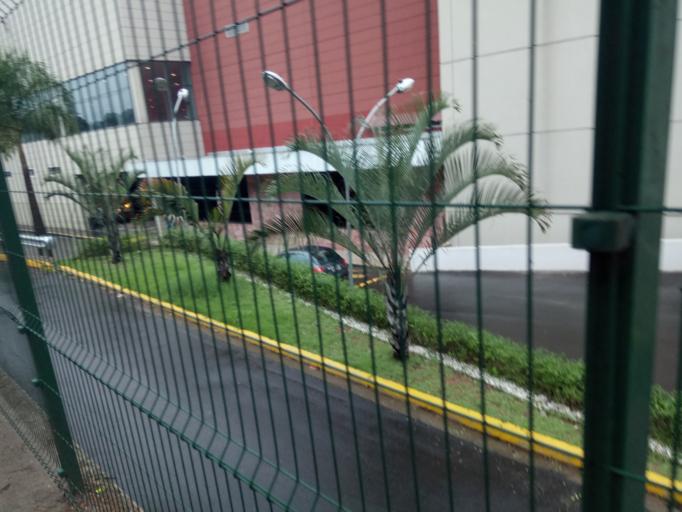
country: BR
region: Sao Paulo
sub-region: Piracicaba
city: Piracicaba
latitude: -22.7031
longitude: -47.6494
